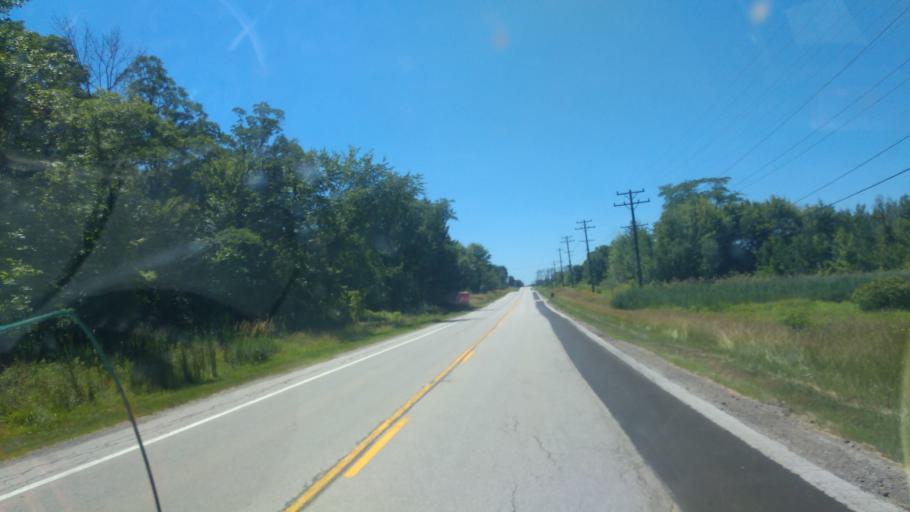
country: US
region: Ohio
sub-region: Ashtabula County
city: Conneaut
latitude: 41.8776
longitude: -80.5723
